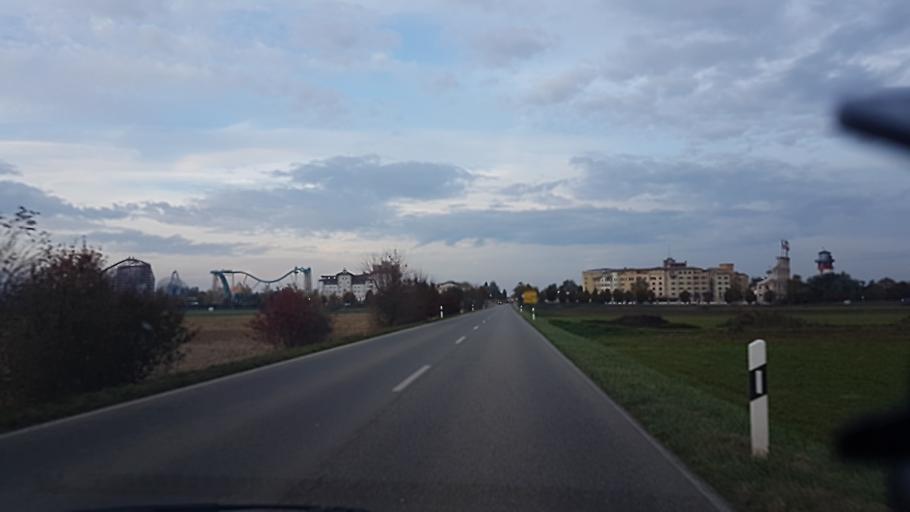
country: DE
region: Baden-Wuerttemberg
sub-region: Freiburg Region
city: Rust
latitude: 48.2563
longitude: 7.7199
